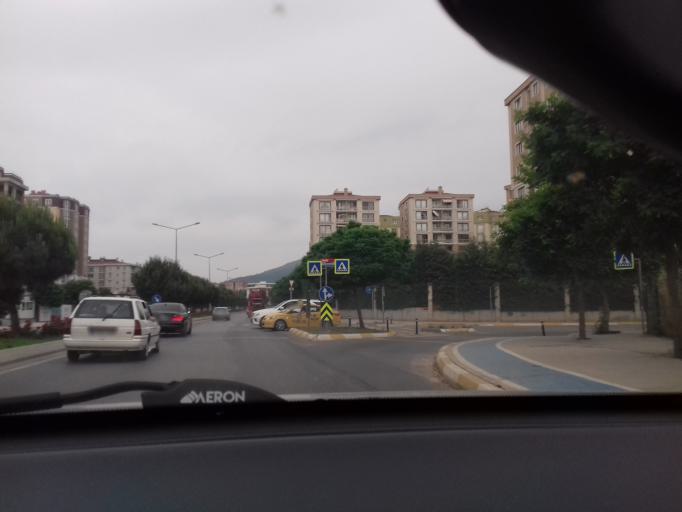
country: TR
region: Istanbul
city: Sultanbeyli
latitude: 40.9314
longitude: 29.3038
